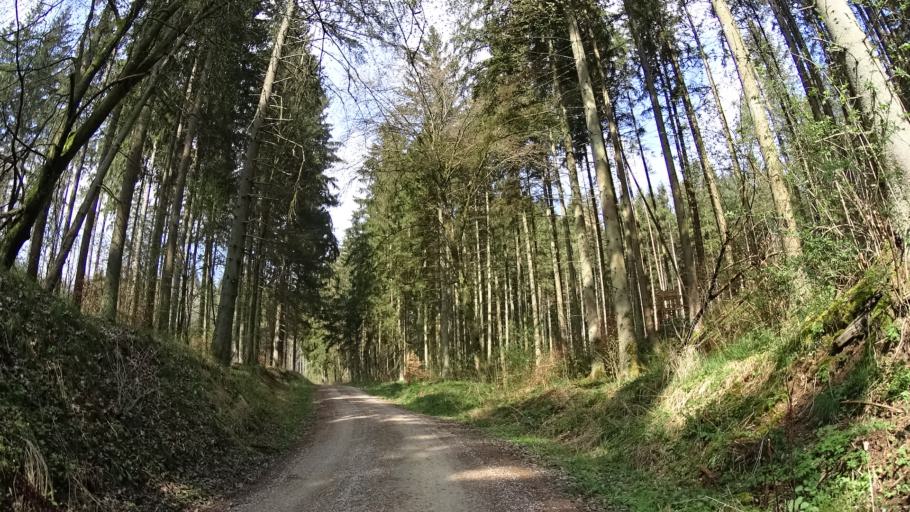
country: DE
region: Bavaria
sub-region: Upper Bavaria
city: Bohmfeld
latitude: 48.8930
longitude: 11.3641
